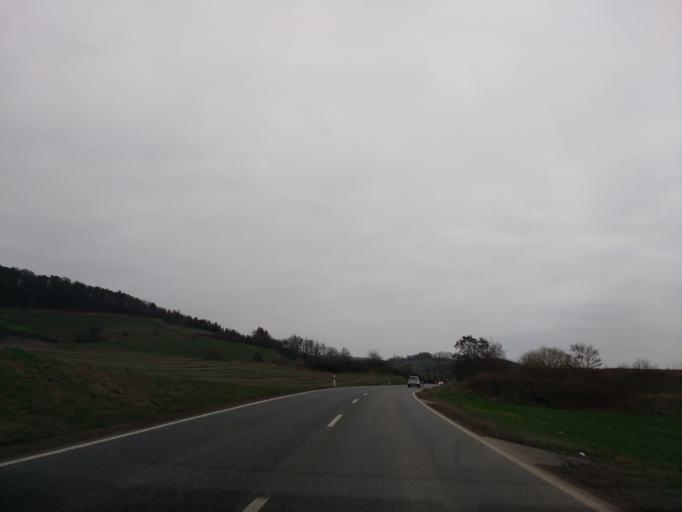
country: DE
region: Hesse
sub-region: Regierungsbezirk Kassel
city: Alheim
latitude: 51.0362
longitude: 9.6791
